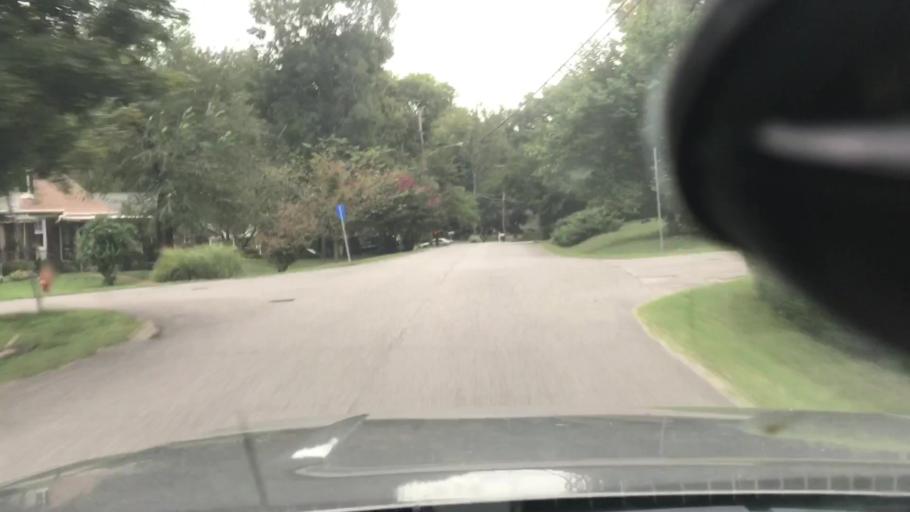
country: US
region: Tennessee
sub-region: Davidson County
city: Oak Hill
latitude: 36.1140
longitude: -86.7801
